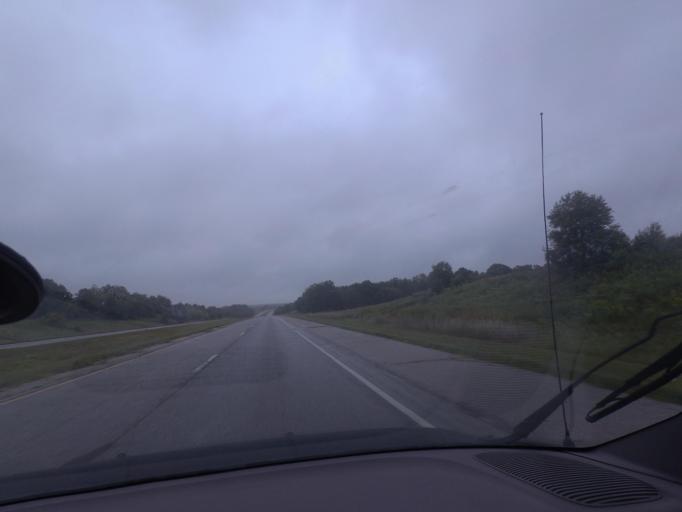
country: US
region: Illinois
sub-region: Pike County
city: Barry
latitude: 39.6928
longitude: -90.9605
